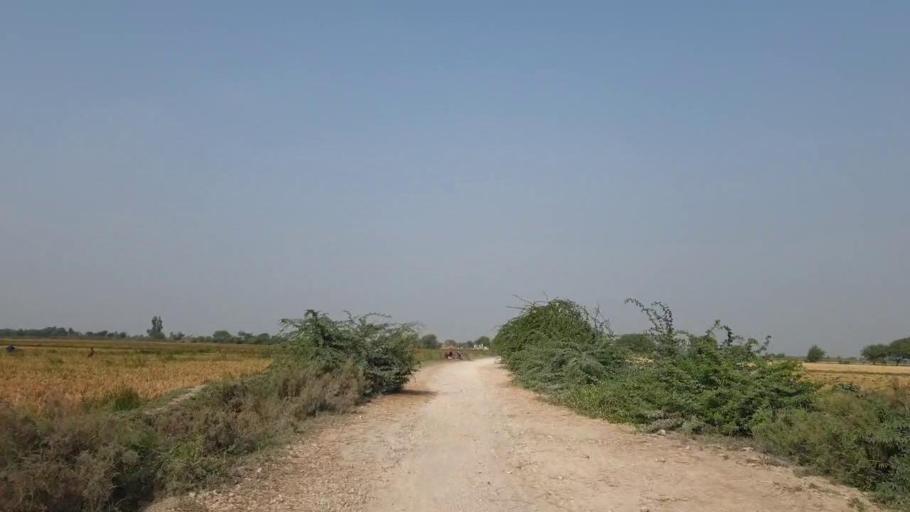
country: PK
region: Sindh
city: Matli
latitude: 24.9432
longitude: 68.5569
